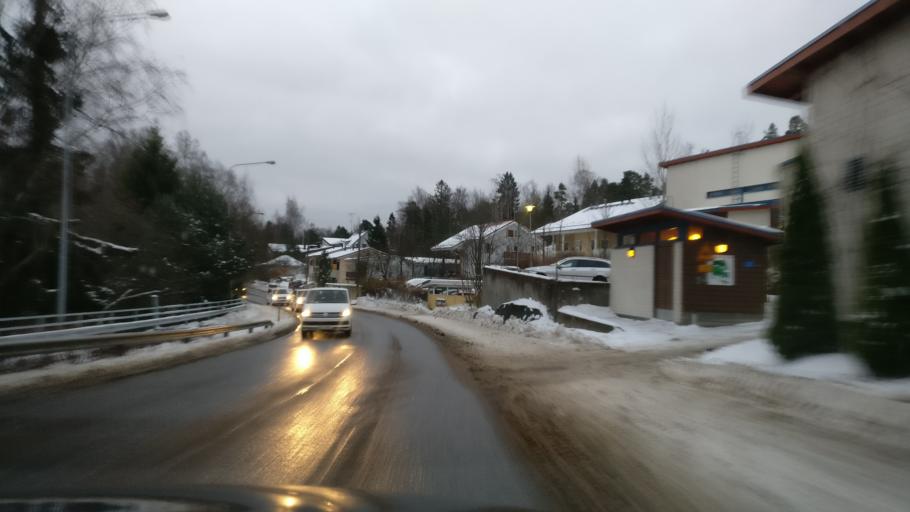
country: FI
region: Uusimaa
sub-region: Helsinki
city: Helsinki
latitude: 60.1679
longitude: 25.0491
